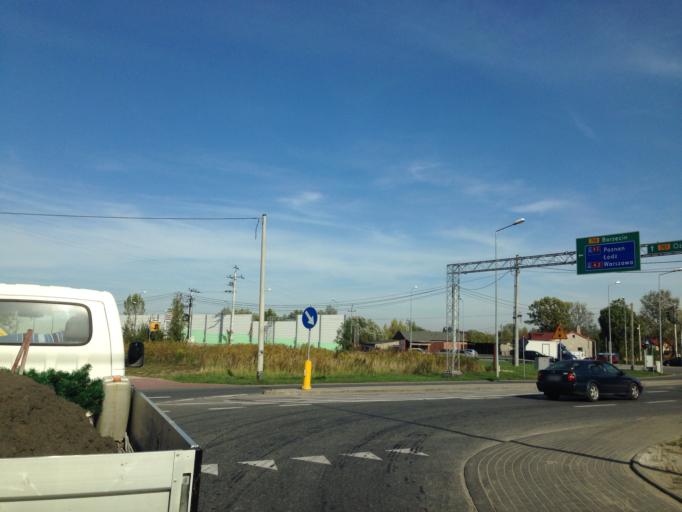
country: PL
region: Masovian Voivodeship
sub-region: Powiat warszawski zachodni
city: Ozarow Mazowiecki
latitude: 52.1826
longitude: 20.7809
